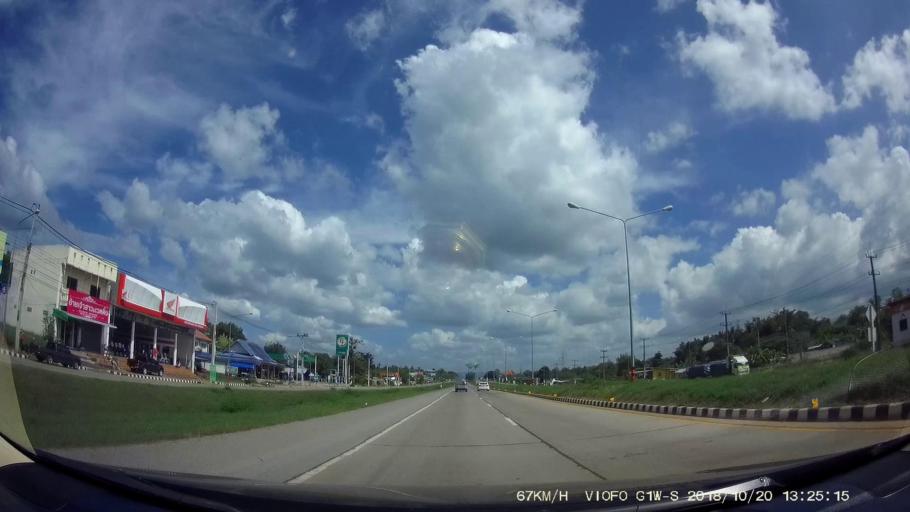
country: TH
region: Chaiyaphum
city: Khon San
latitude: 16.5951
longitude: 101.9300
